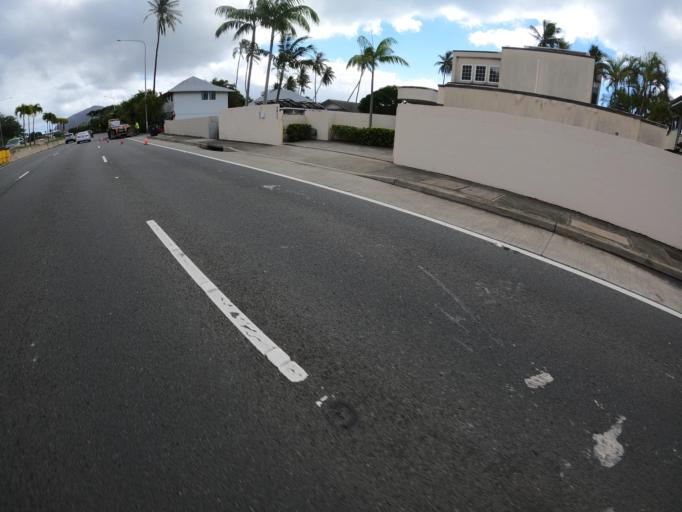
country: US
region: Hawaii
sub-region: Honolulu County
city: Waimanalo Beach
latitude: 21.2822
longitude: -157.7326
